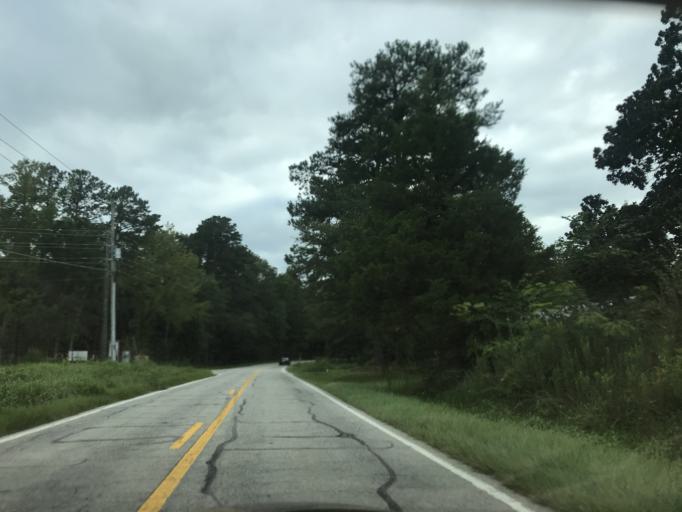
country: US
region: North Carolina
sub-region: Wake County
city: Garner
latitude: 35.5744
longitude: -78.5857
